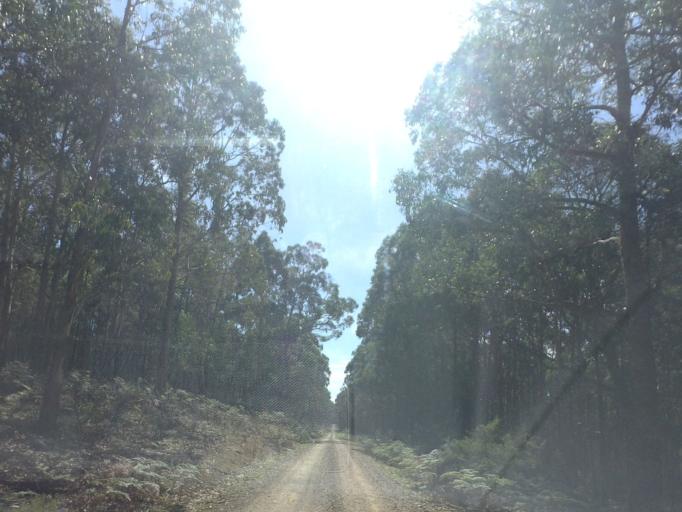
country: AU
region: Victoria
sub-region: Moorabool
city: Bacchus Marsh
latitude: -37.4403
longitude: 144.3783
